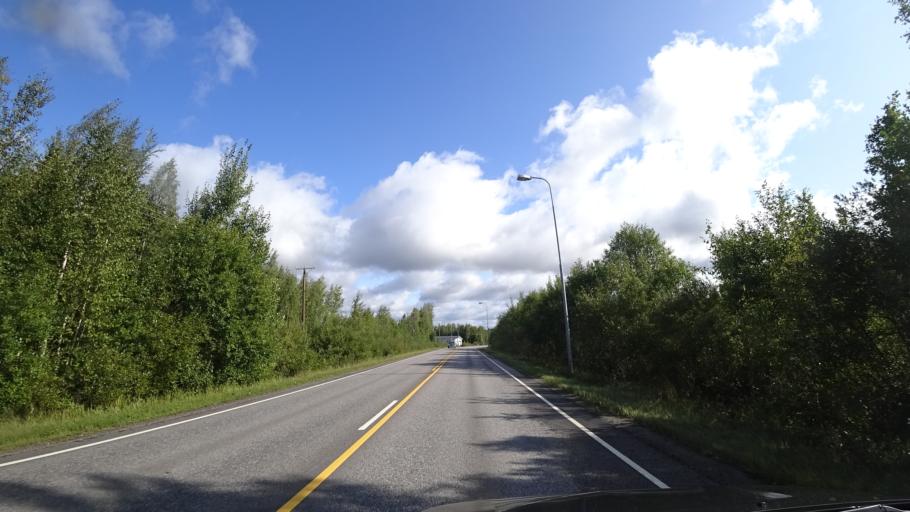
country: FI
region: Uusimaa
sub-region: Helsinki
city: Hyvinge
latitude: 60.5480
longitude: 24.9409
